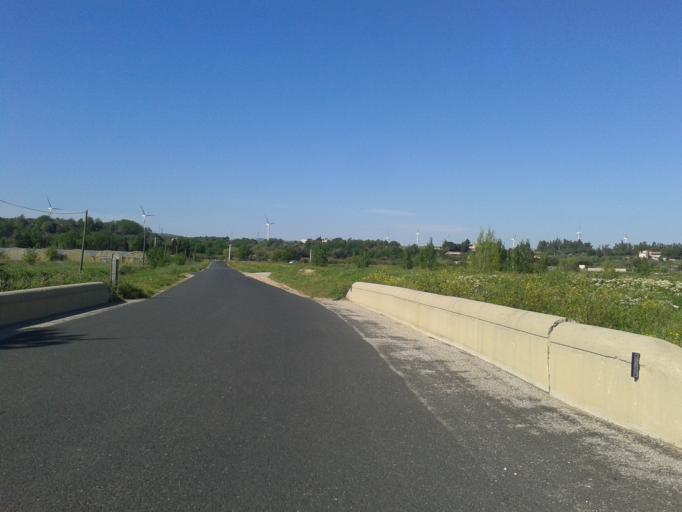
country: FR
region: Languedoc-Roussillon
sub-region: Departement des Pyrenees-Orientales
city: Pezilla-la-Riviere
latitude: 42.6978
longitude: 2.7591
